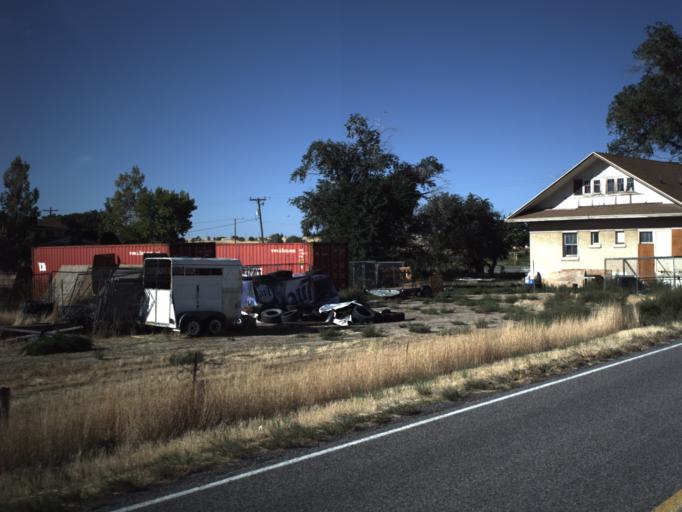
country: US
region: Utah
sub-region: Millard County
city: Delta
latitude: 39.5362
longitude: -112.2725
